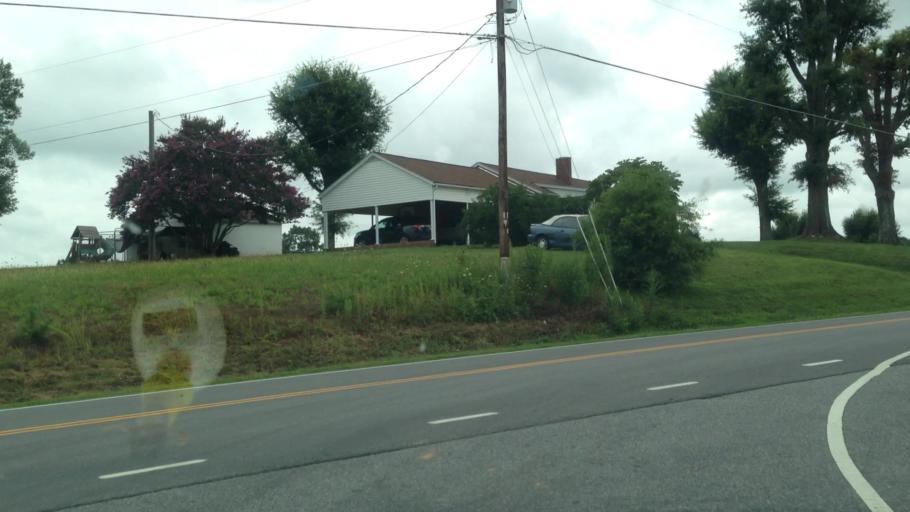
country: US
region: North Carolina
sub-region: Rockingham County
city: Mayodan
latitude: 36.4210
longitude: -80.0836
